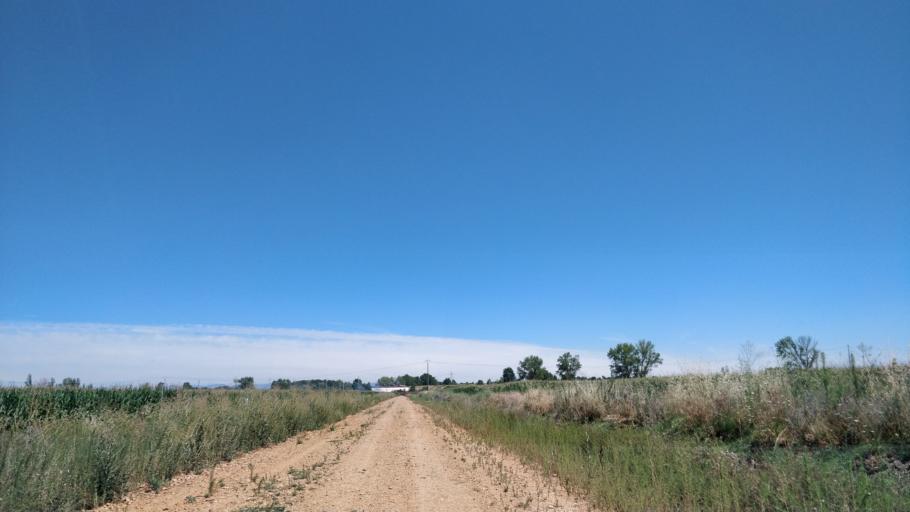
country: ES
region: Castille and Leon
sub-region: Provincia de Leon
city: Bustillo del Paramo
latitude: 42.4725
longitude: -5.8124
